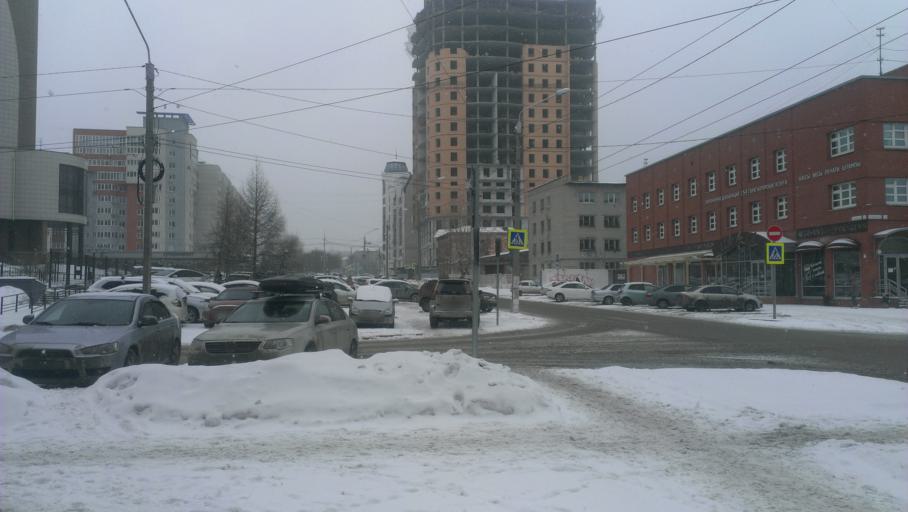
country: RU
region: Altai Krai
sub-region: Gorod Barnaulskiy
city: Barnaul
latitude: 53.3372
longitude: 83.7828
